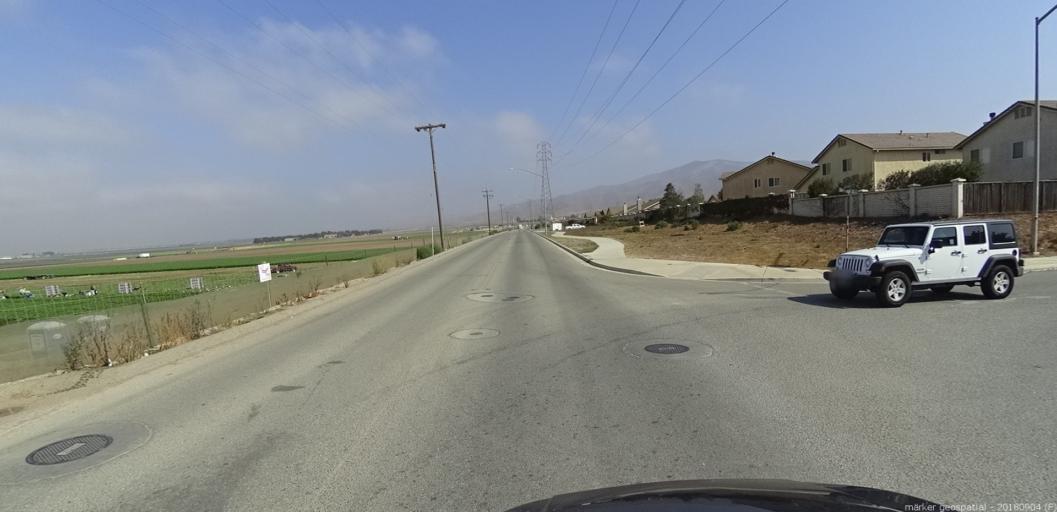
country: US
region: California
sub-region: Monterey County
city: Soledad
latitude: 36.4401
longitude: -121.3336
